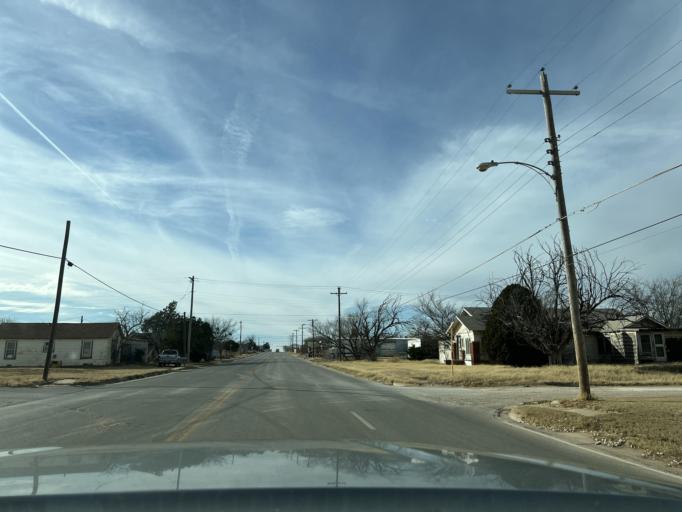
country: US
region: Texas
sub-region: Jones County
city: Anson
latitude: 32.7515
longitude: -99.8918
